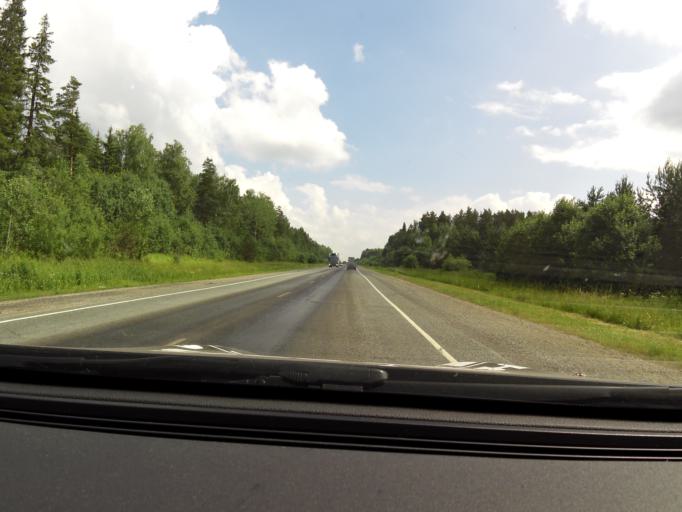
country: RU
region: Sverdlovsk
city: Achit
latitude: 56.8410
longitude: 57.7525
